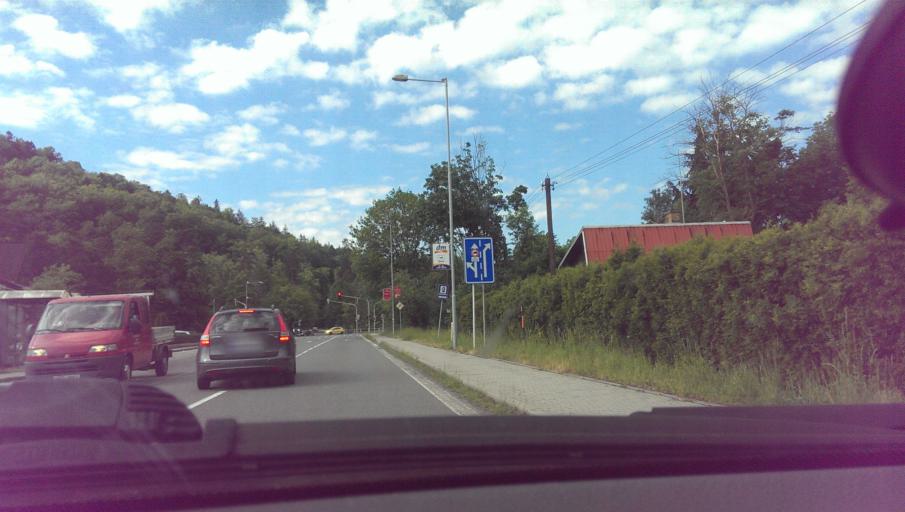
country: CZ
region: Zlin
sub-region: Okres Vsetin
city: Roznov pod Radhostem
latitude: 49.4666
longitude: 18.1577
